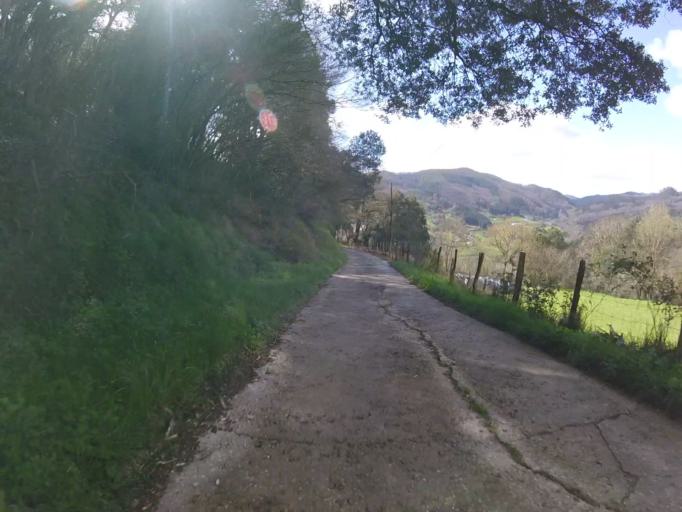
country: ES
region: Basque Country
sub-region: Provincia de Guipuzcoa
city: Albiztur
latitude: 43.1350
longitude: -2.1272
